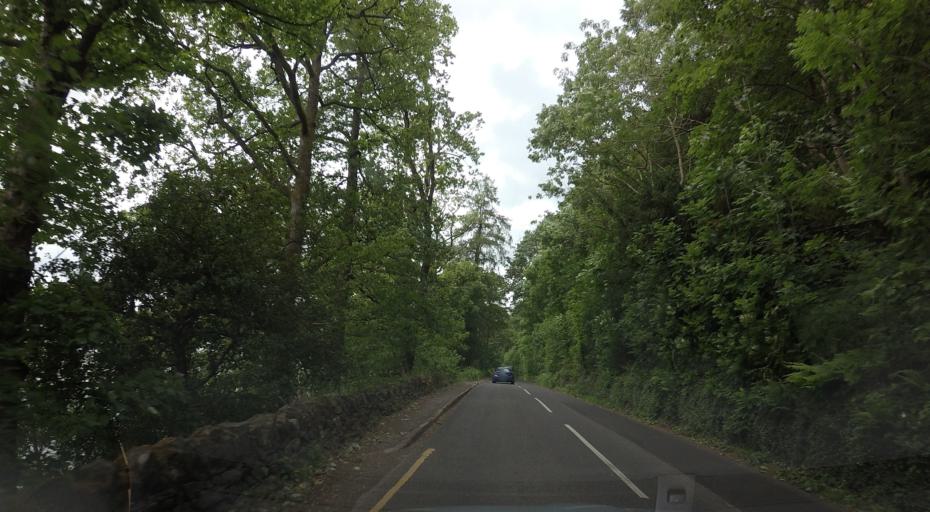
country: GB
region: England
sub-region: Cumbria
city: Keswick
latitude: 54.5739
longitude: -3.1322
